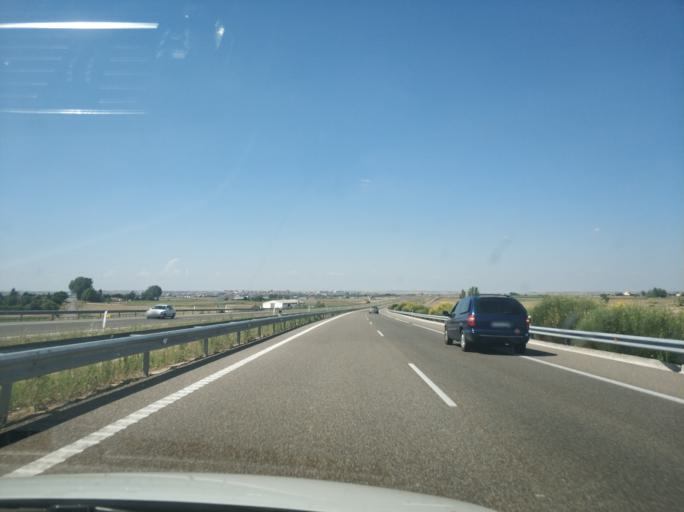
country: ES
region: Castille and Leon
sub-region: Provincia de Zamora
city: Morales del Vino
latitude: 41.4575
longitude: -5.7222
